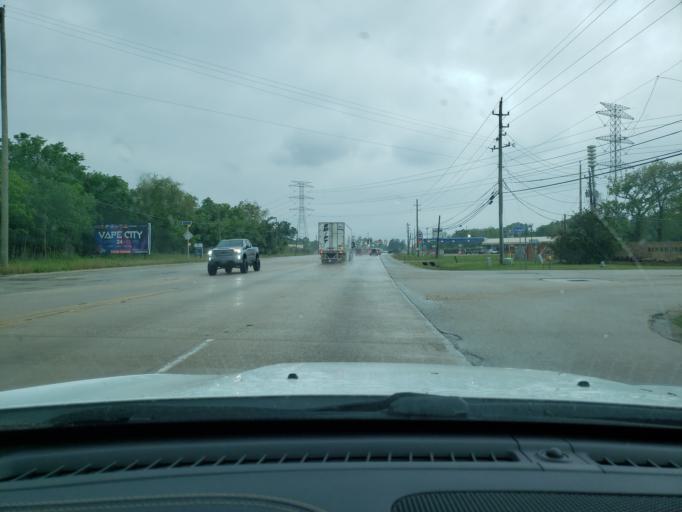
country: US
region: Texas
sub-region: Chambers County
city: Mont Belvieu
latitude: 29.7999
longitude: -94.9050
